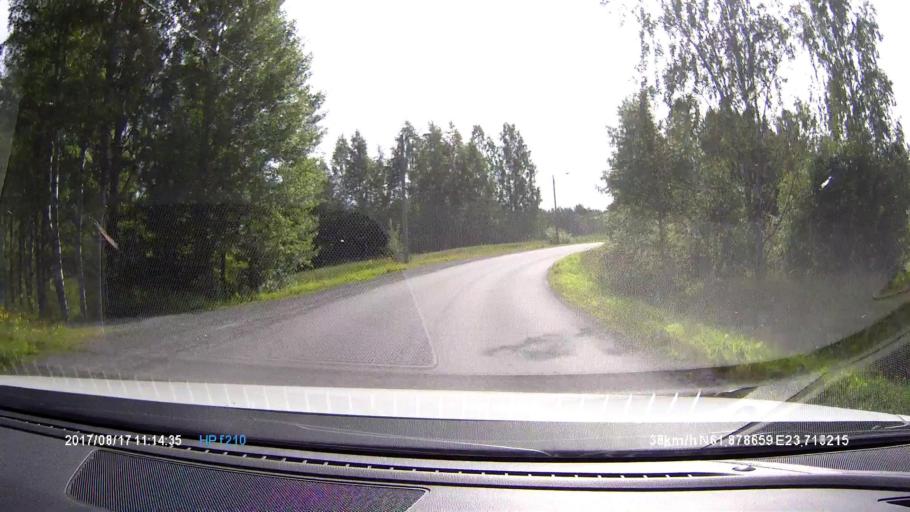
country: FI
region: Pirkanmaa
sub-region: Tampere
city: Kuru
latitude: 61.8787
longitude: 23.7181
